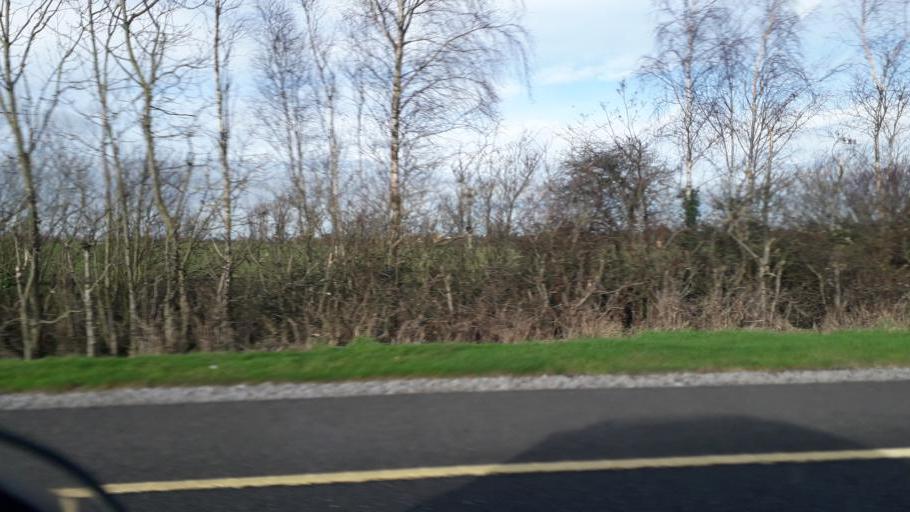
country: IE
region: Leinster
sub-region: Lu
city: Castlebellingham
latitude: 53.8956
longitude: -6.4243
